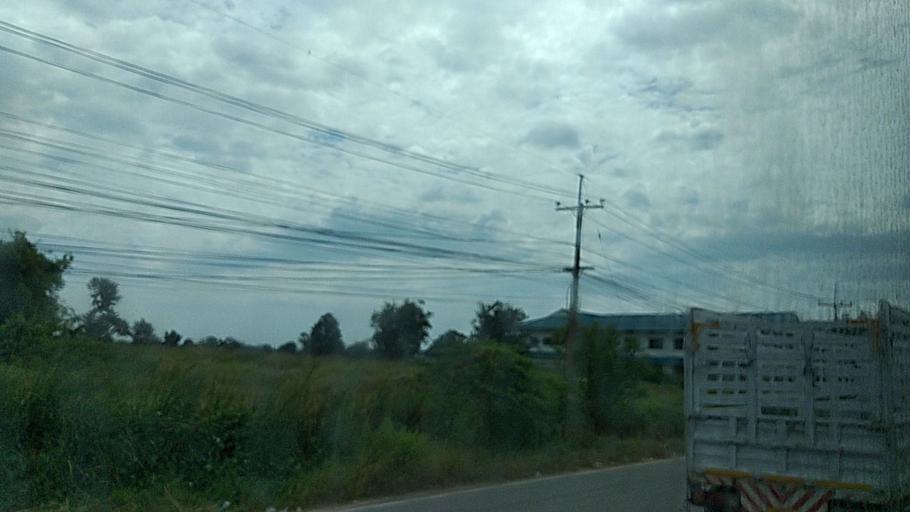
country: TH
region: Maha Sarakham
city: Kantharawichai
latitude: 16.2713
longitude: 103.2872
